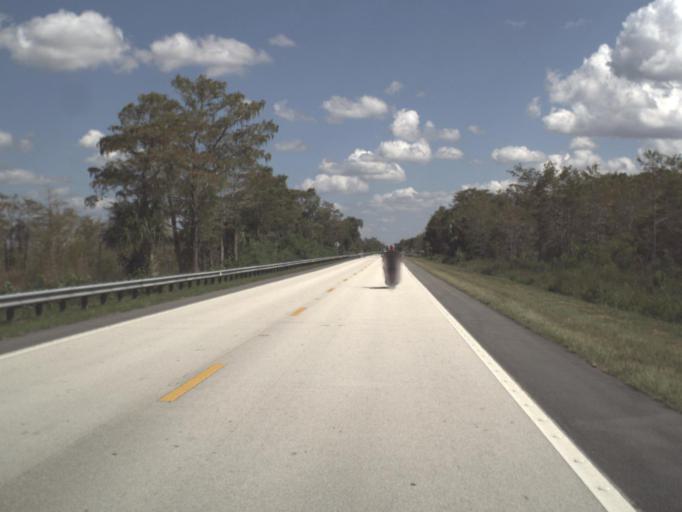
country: US
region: Florida
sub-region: Collier County
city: Immokalee
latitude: 25.8627
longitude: -81.0913
